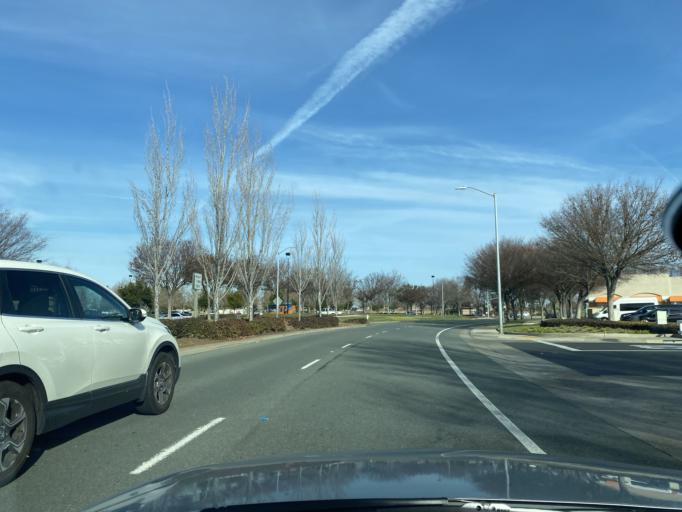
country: US
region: California
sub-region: Sacramento County
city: Laguna
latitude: 38.4241
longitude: -121.4004
